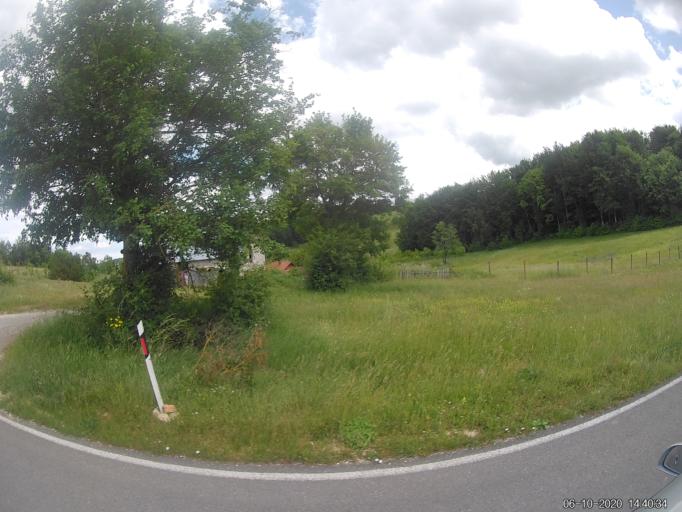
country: XK
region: Prizren
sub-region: Komuna e Therandes
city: Budakovo
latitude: 42.3954
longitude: 20.9433
